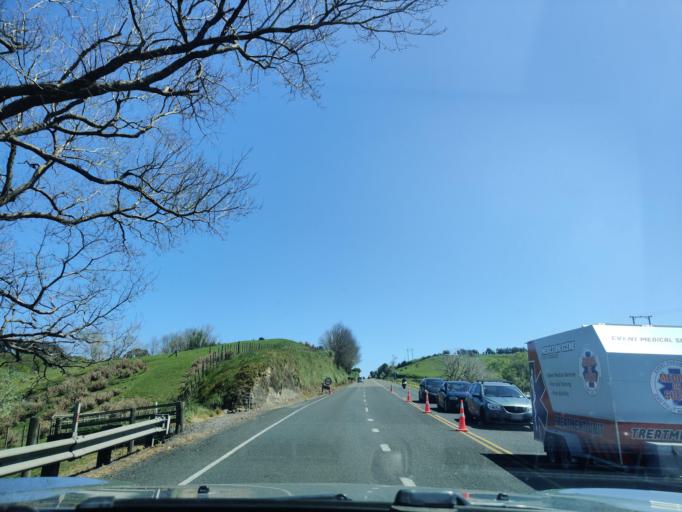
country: NZ
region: Taranaki
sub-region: South Taranaki District
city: Hawera
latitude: -39.6180
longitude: 174.3421
